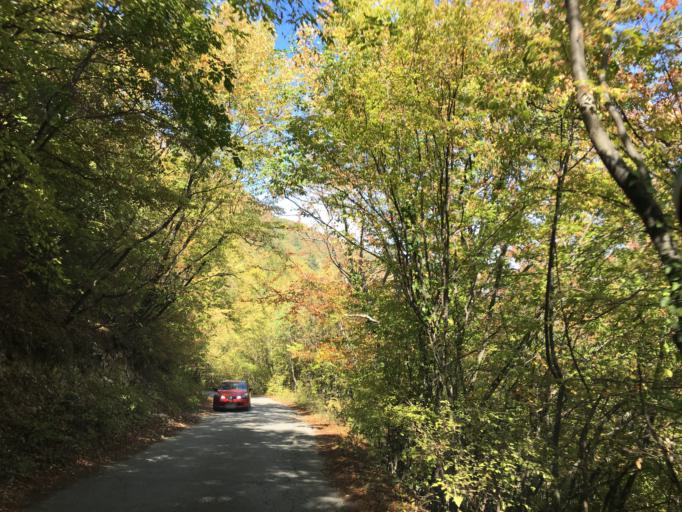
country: BG
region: Pazardzhik
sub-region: Obshtina Peshtera
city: Peshtera
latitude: 42.0071
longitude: 24.2787
